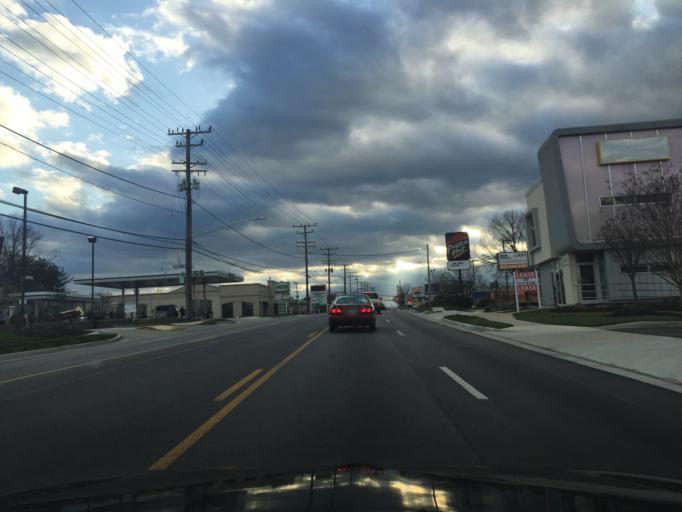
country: US
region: Maryland
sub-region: Baltimore County
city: Parkville
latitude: 39.3968
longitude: -76.5654
